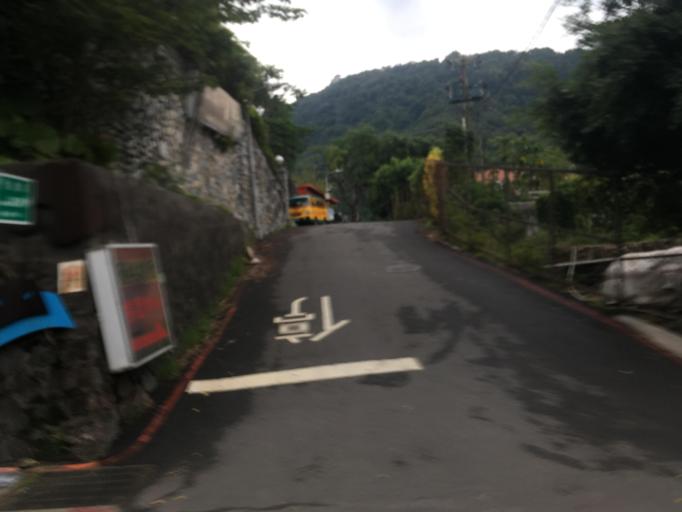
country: TW
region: Taipei
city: Taipei
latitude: 25.1362
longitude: 121.5288
